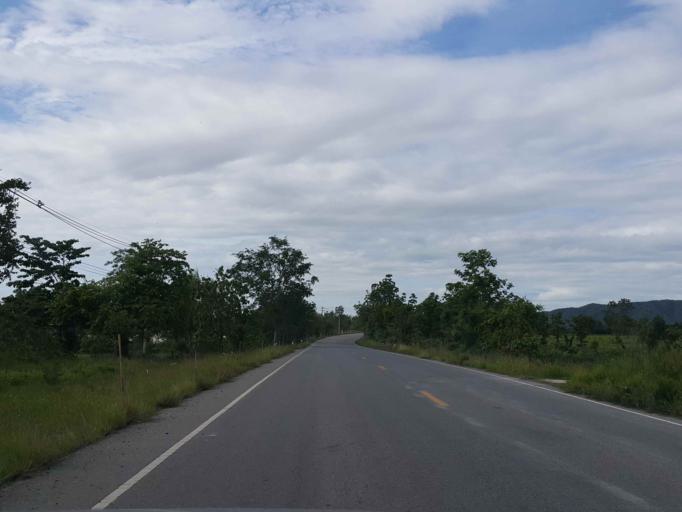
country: TH
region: Sukhothai
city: Thung Saliam
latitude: 17.2385
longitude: 99.5156
